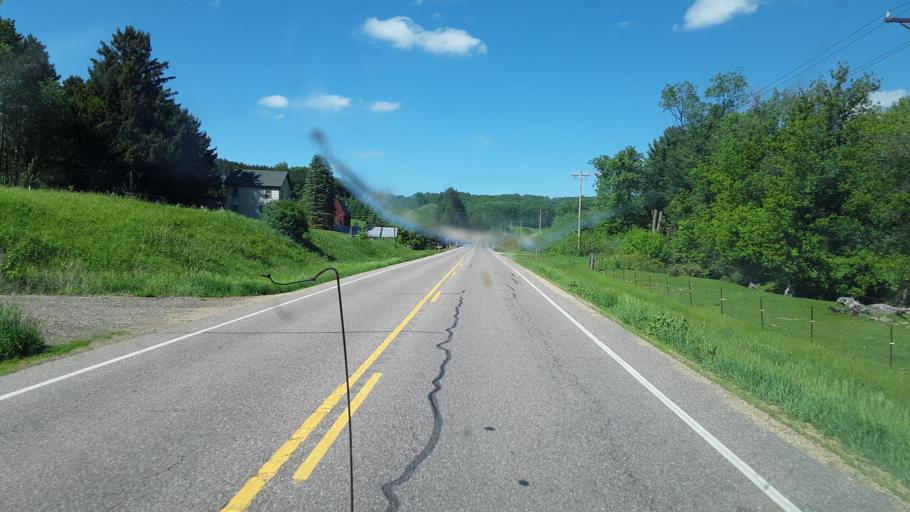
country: US
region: Wisconsin
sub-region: Sauk County
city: Reedsburg
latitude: 43.6085
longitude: -90.1227
